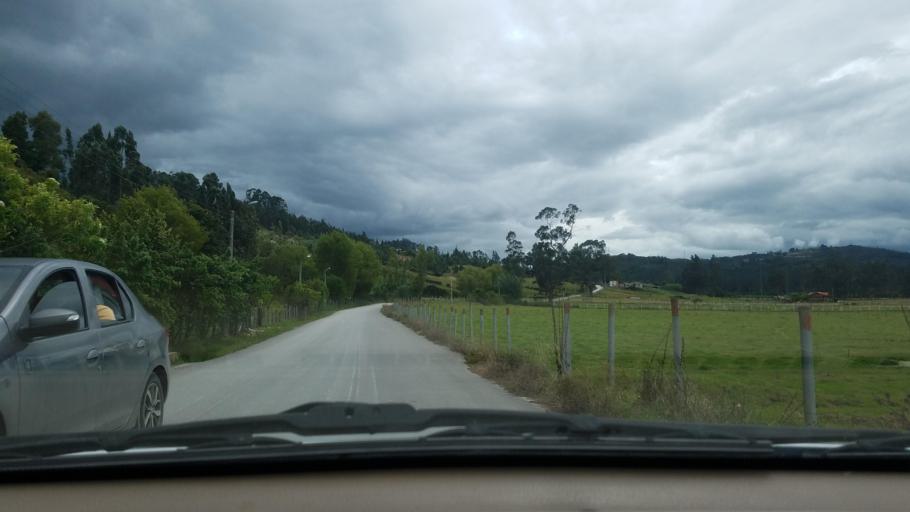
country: CO
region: Boyaca
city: Paipa
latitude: 5.7495
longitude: -73.1075
